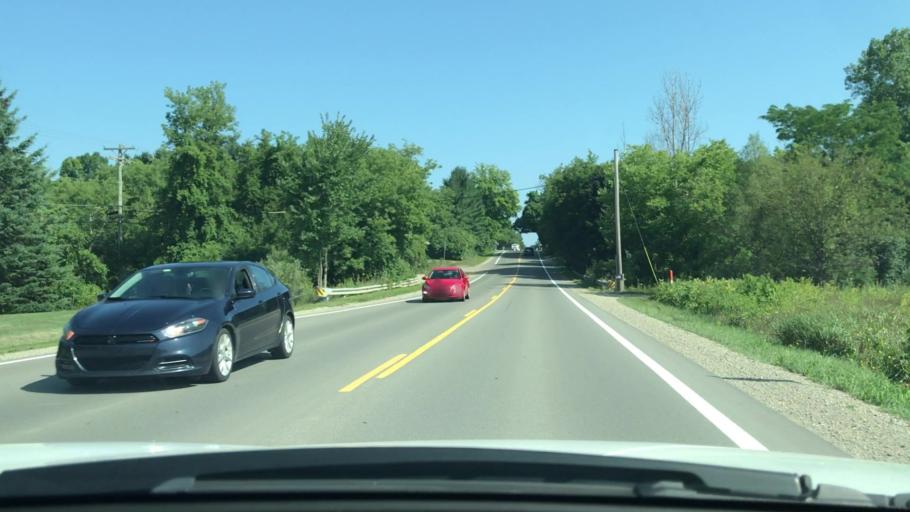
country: US
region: Michigan
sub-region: Oakland County
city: Oxford
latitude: 42.7967
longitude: -83.3331
